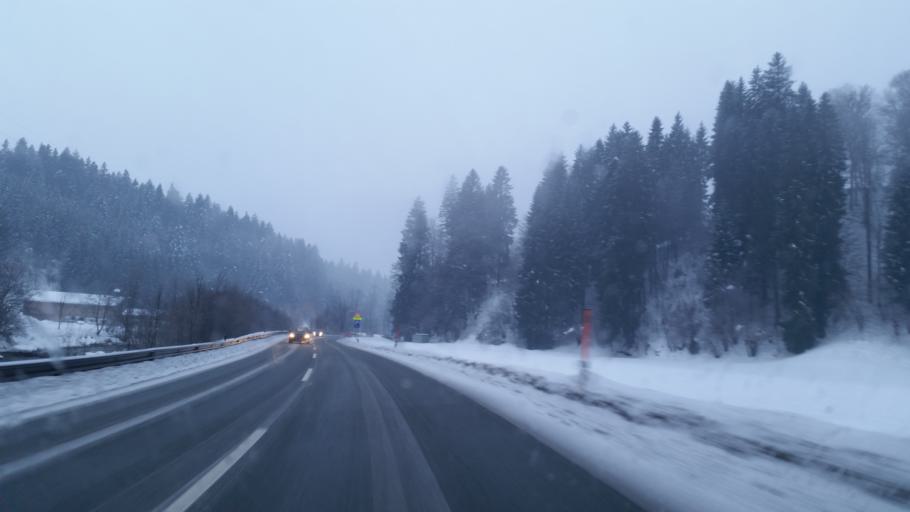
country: AT
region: Tyrol
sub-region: Politischer Bezirk Kitzbuhel
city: Oberndorf in Tirol
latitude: 47.5229
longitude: 12.3849
